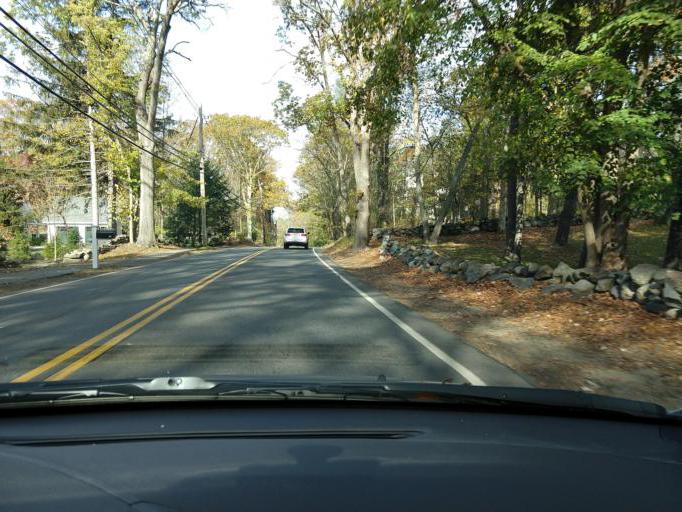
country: US
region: Massachusetts
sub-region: Middlesex County
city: Concord
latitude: 42.4693
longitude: -71.3605
